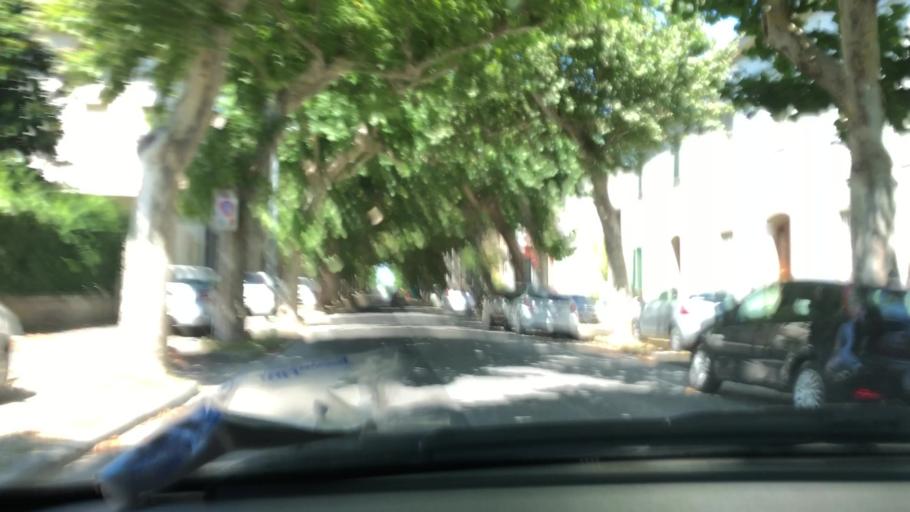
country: IT
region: Tuscany
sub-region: Province of Pisa
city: Pontedera
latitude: 43.6606
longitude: 10.6363
